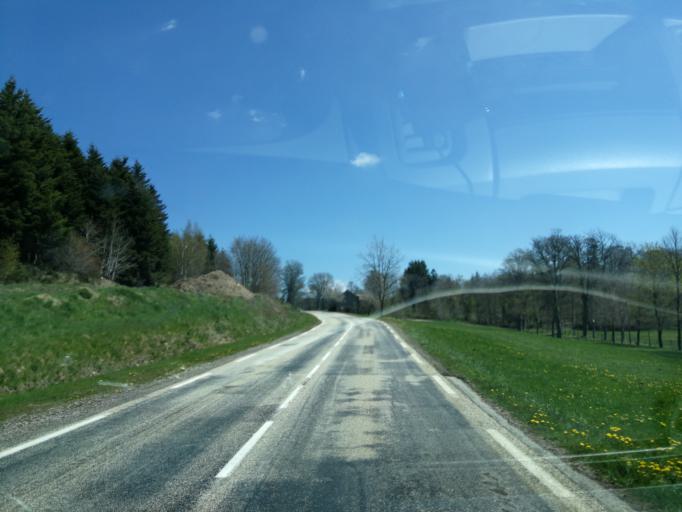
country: FR
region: Rhone-Alpes
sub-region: Departement de l'Ardeche
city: Saint-Agreve
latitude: 45.0174
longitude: 4.4036
